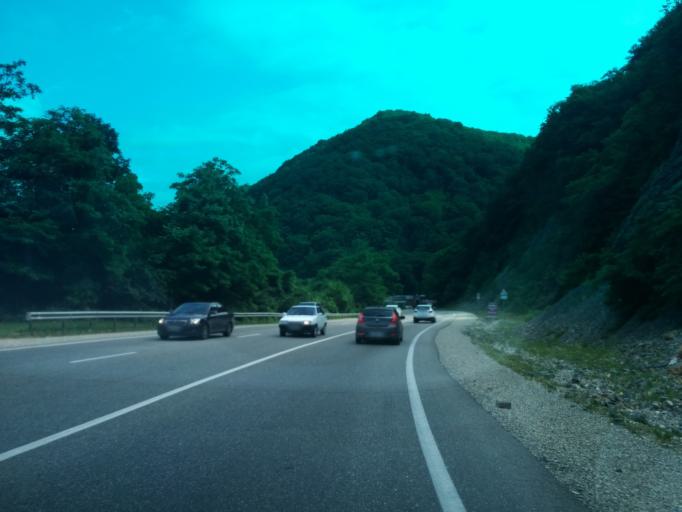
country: RU
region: Krasnodarskiy
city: Nebug
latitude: 44.1740
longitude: 38.9758
